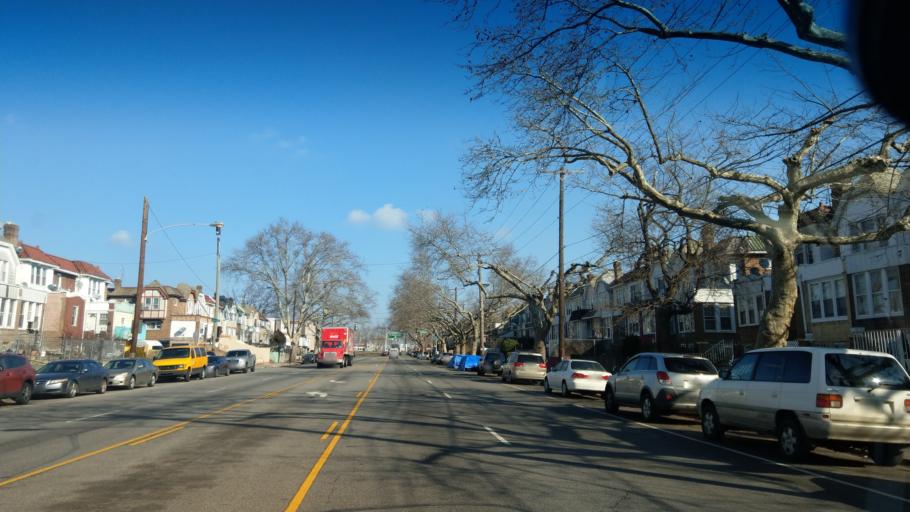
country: US
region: Pennsylvania
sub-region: Montgomery County
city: Rockledge
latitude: 40.0269
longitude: -75.1076
